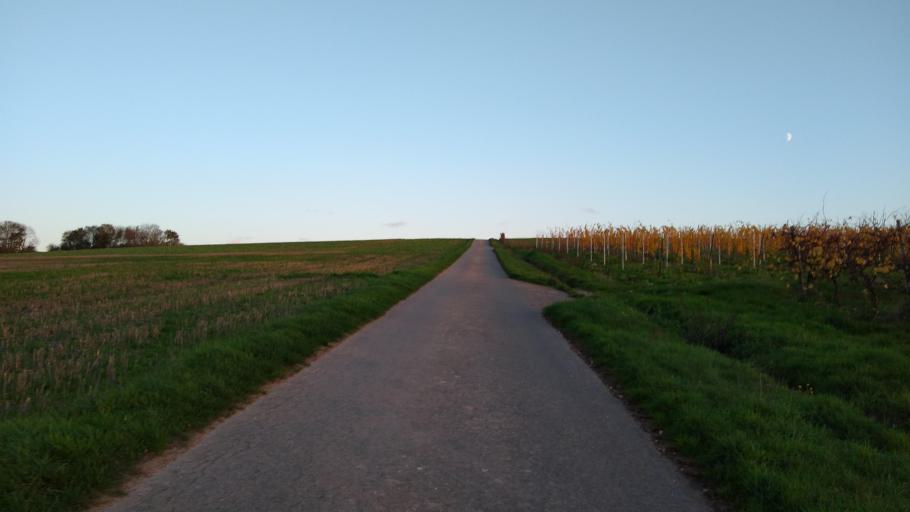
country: DE
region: Rheinland-Pfalz
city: Bekond
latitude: 49.8561
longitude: 6.8181
